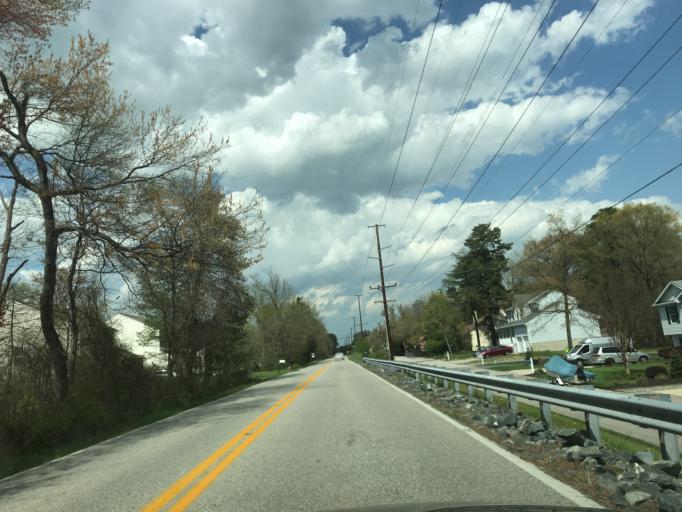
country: US
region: Maryland
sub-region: Anne Arundel County
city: Severn
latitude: 39.1228
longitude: -76.6785
